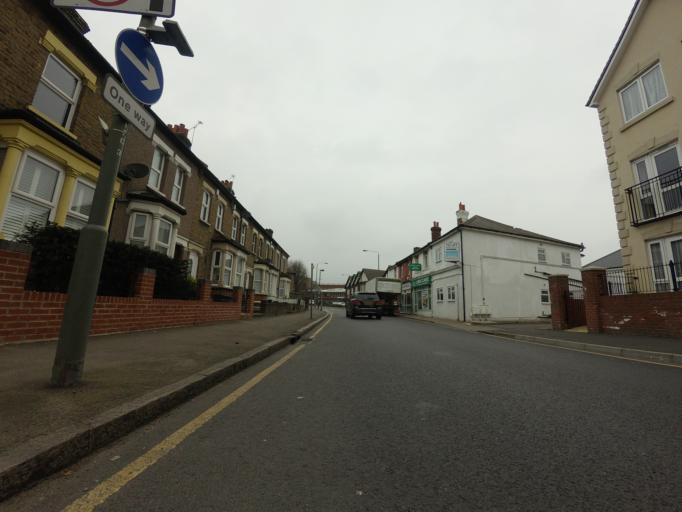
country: GB
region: England
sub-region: Greater London
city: Orpington
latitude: 51.3806
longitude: 0.1027
